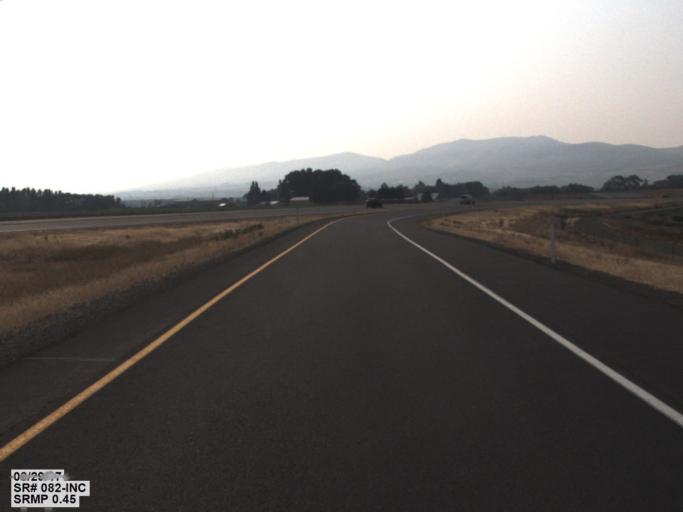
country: US
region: Washington
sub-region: Kittitas County
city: Ellensburg
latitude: 46.9647
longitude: -120.5087
